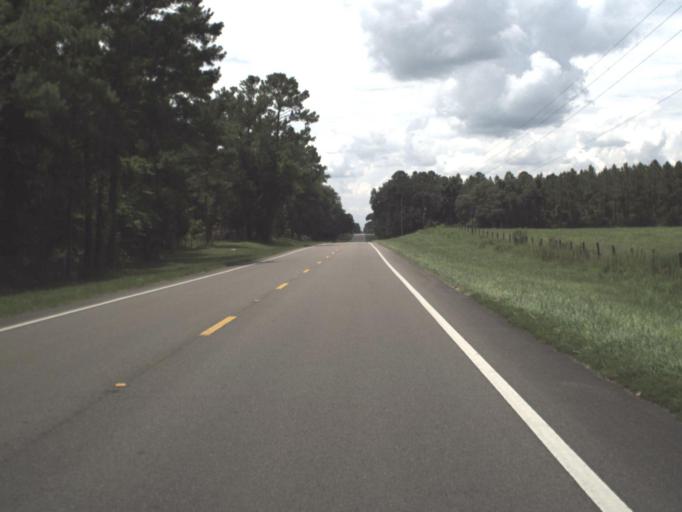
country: US
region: Florida
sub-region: Levy County
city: Williston
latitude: 29.4297
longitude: -82.4596
